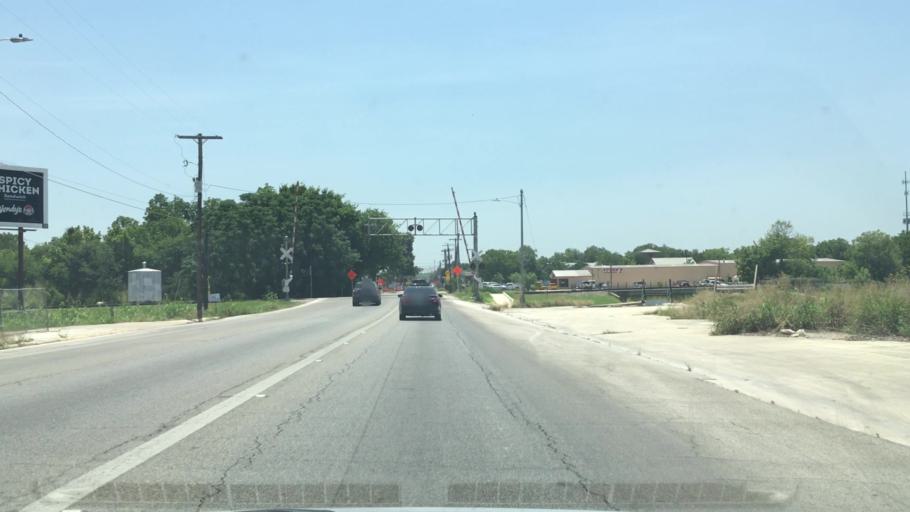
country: US
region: Texas
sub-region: Hays County
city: San Marcos
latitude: 29.8792
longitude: -97.9409
